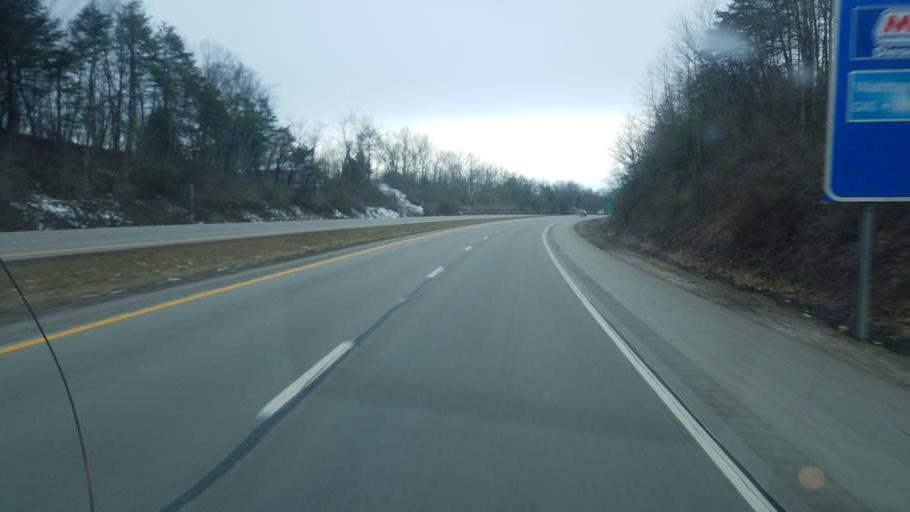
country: US
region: West Virginia
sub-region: Wood County
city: Mineral Wells
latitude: 39.2057
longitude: -81.5204
